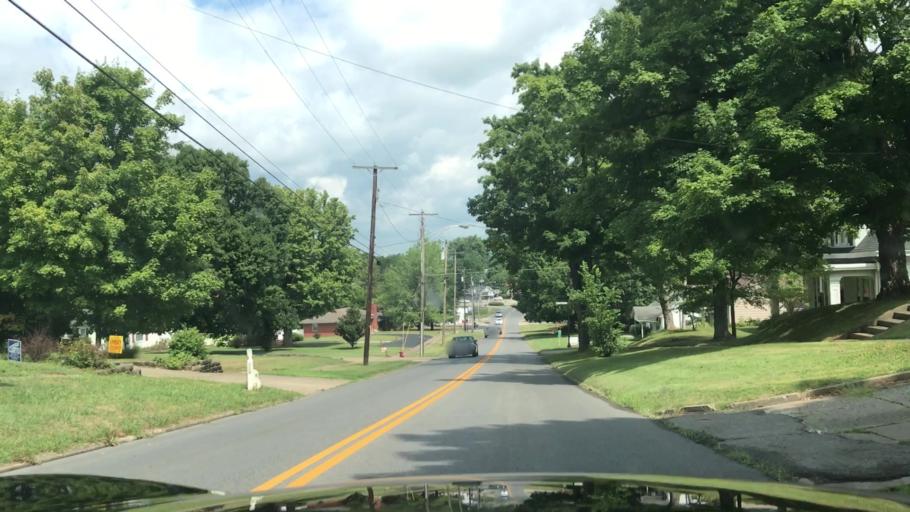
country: US
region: Kentucky
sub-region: Muhlenberg County
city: Greenville
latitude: 37.2070
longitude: -87.1794
